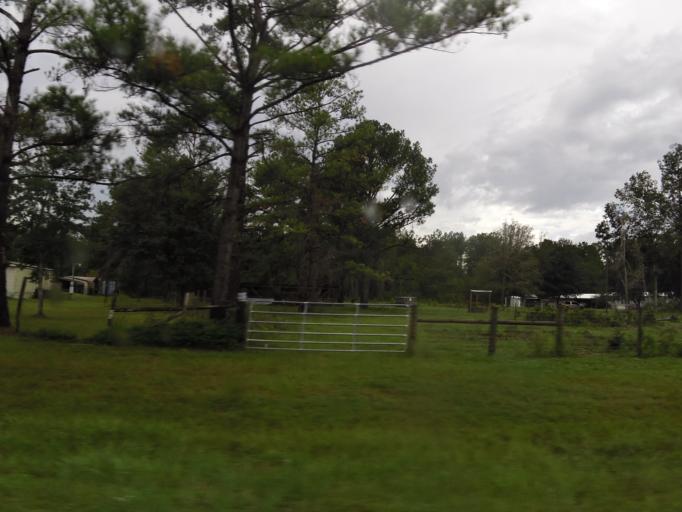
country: US
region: Florida
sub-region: Duval County
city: Baldwin
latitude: 30.4167
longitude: -82.0269
